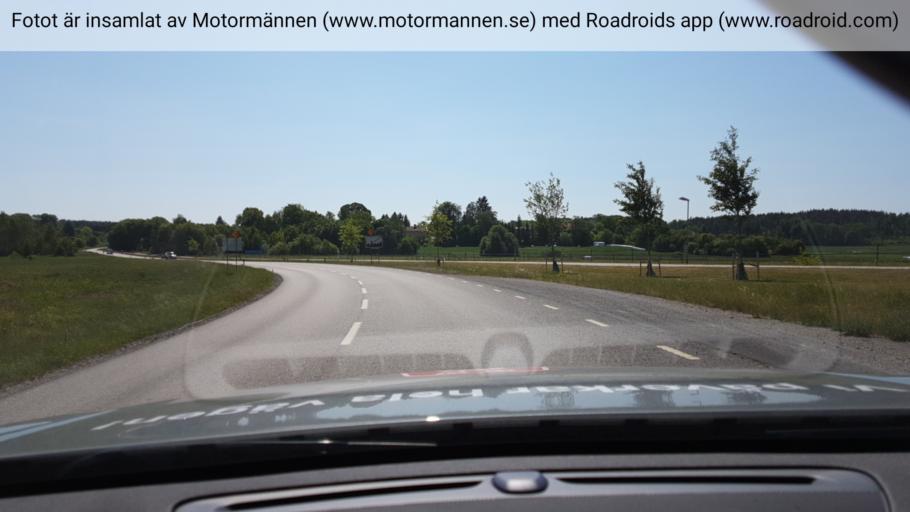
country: SE
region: Stockholm
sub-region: Norrtalje Kommun
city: Rimbo
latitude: 59.7368
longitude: 18.3696
